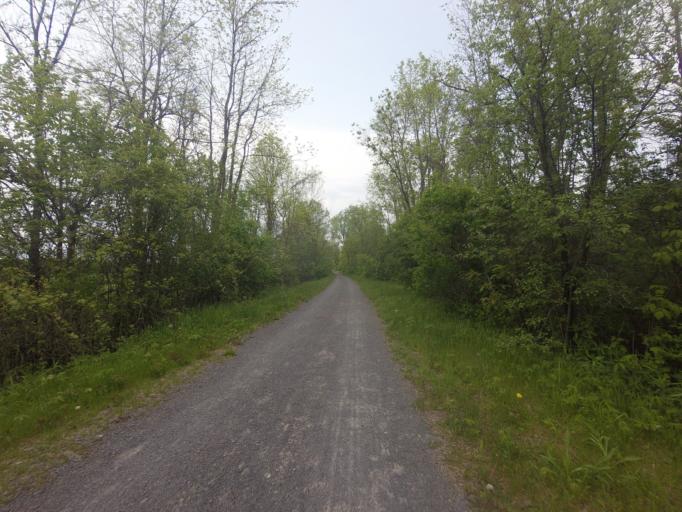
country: CA
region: Ontario
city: Kingston
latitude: 44.2911
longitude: -76.5585
